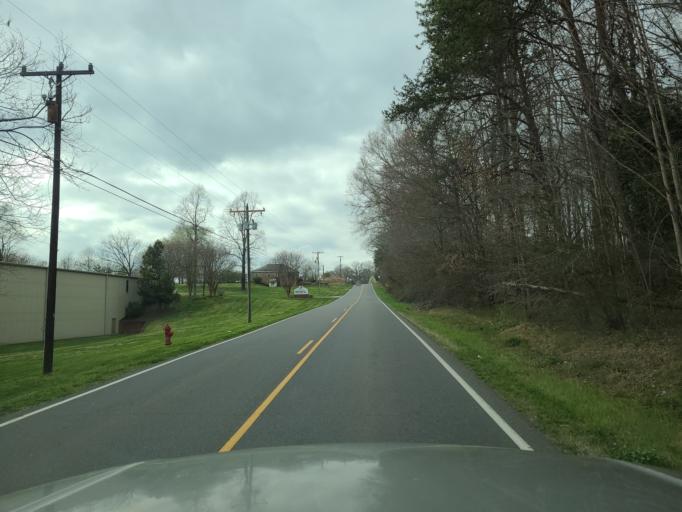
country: US
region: North Carolina
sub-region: Cleveland County
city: Boiling Springs
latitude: 35.2537
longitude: -81.6826
